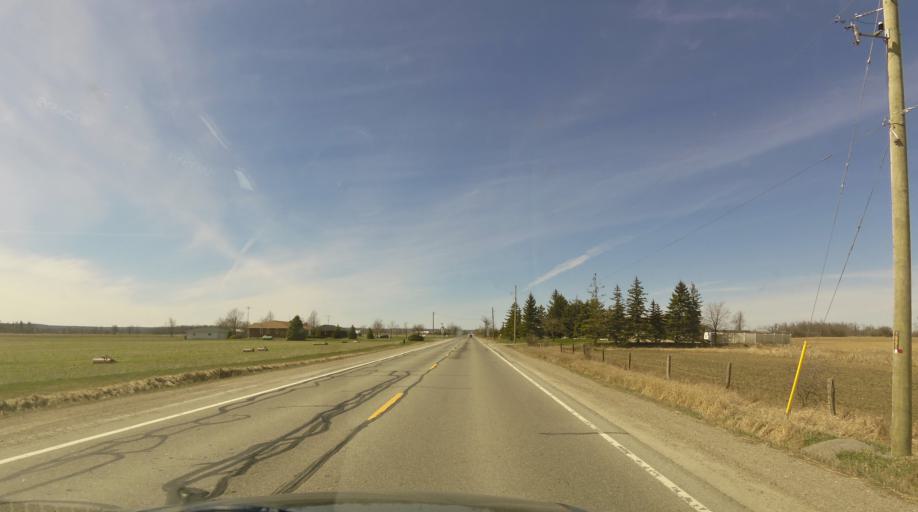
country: CA
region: Ontario
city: Brampton
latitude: 43.7010
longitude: -79.8758
